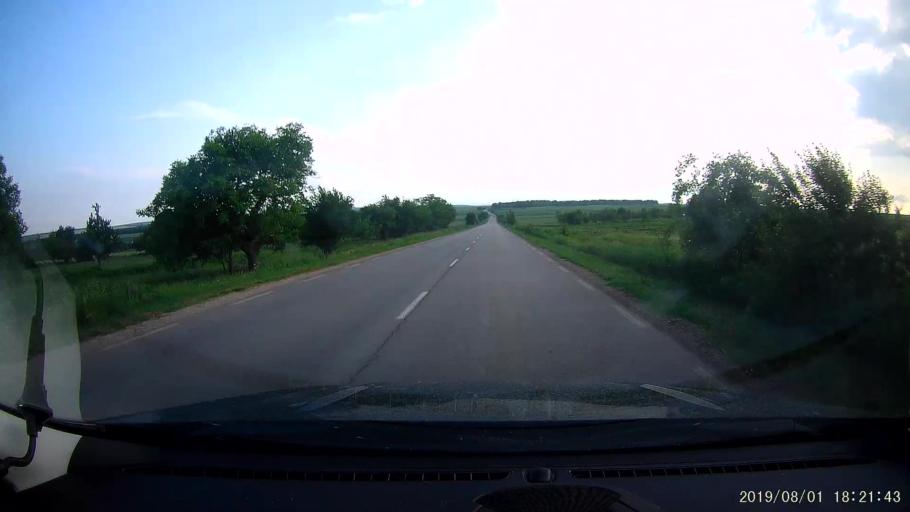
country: BG
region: Shumen
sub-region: Obshtina Kaolinovo
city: Kaolinovo
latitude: 43.6489
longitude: 27.0668
